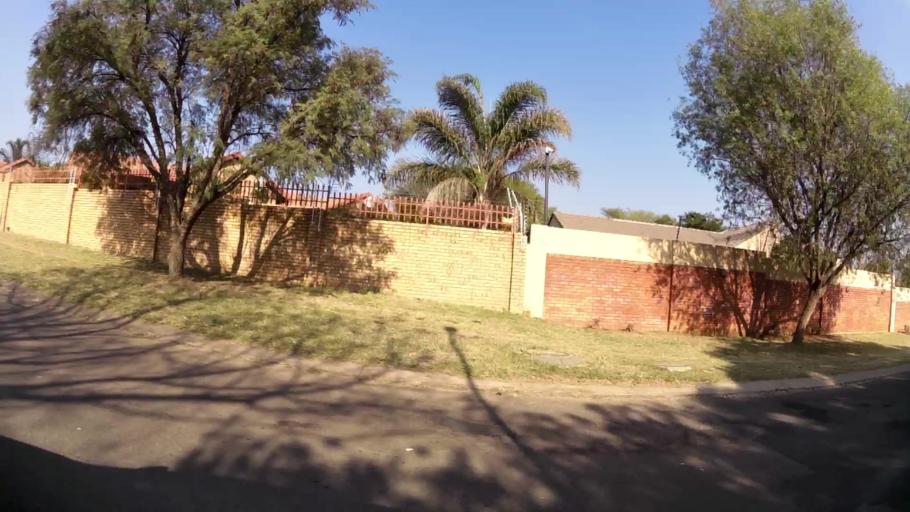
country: ZA
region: Gauteng
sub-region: City of Tshwane Metropolitan Municipality
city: Pretoria
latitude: -25.7648
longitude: 28.3338
